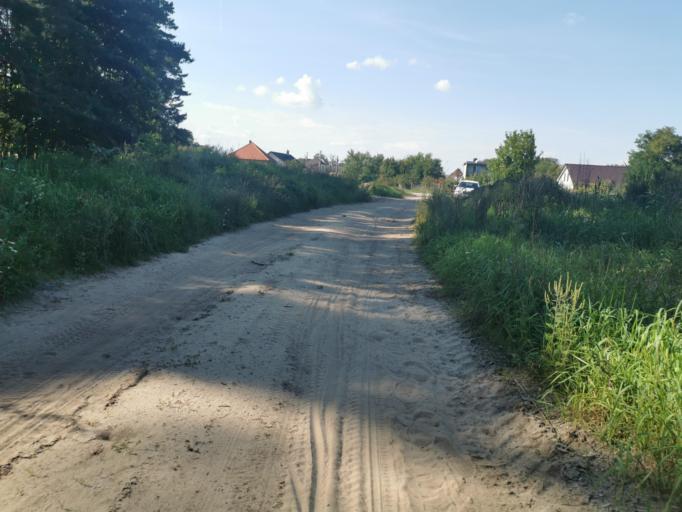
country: SK
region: Trnavsky
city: Gbely
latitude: 48.6324
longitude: 17.2264
